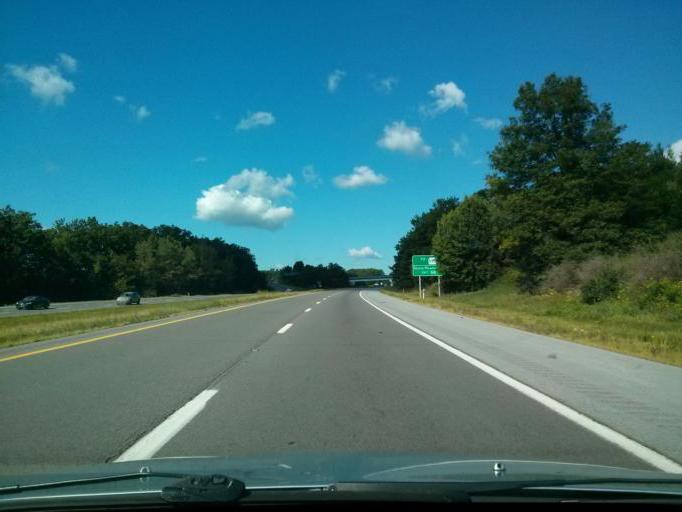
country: US
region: Pennsylvania
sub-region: Centre County
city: Park Forest Village
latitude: 40.8158
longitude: -77.9135
